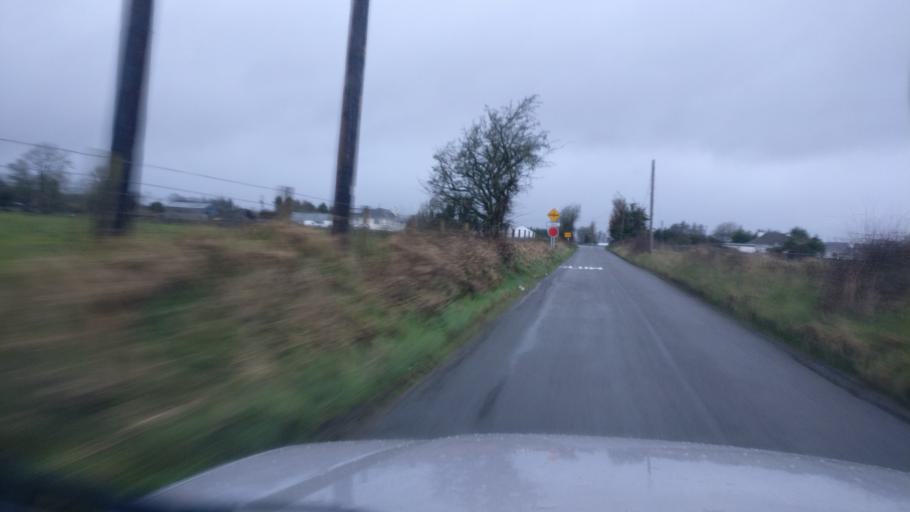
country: IE
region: Connaught
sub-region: County Galway
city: Loughrea
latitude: 53.2671
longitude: -8.4072
